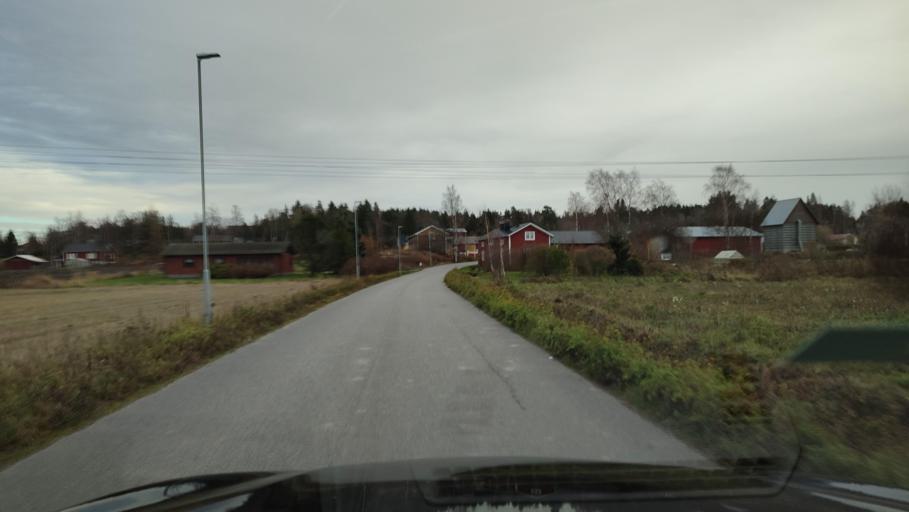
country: FI
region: Ostrobothnia
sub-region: Sydosterbotten
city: Naerpes
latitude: 62.4665
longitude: 21.3631
